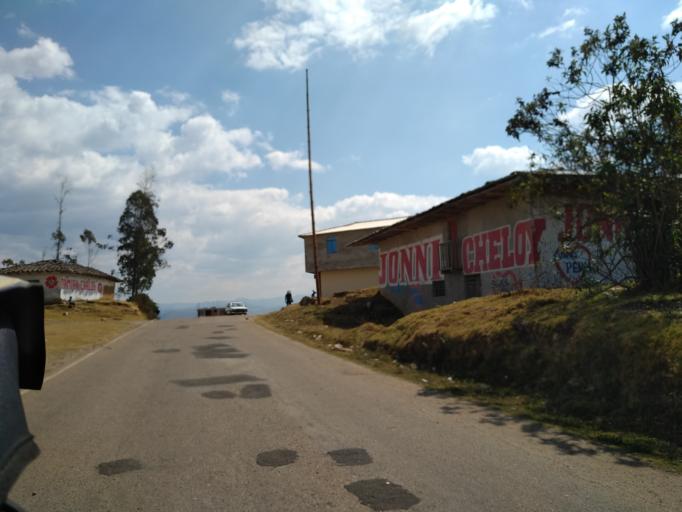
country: PE
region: Cajamarca
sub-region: Provincia de Celendin
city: Celendin
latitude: -6.8762
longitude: -78.1142
